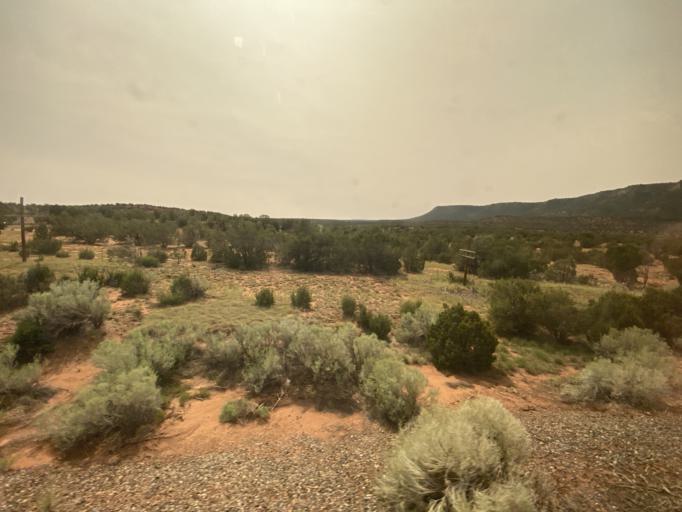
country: US
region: New Mexico
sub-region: San Miguel County
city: Pecos
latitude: 35.3928
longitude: -105.4835
